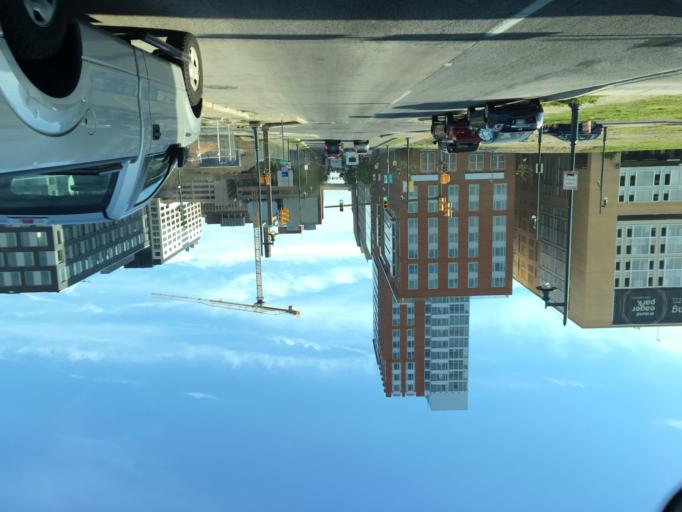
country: US
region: Maryland
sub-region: City of Baltimore
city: Baltimore
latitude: 39.3024
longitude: -76.5912
